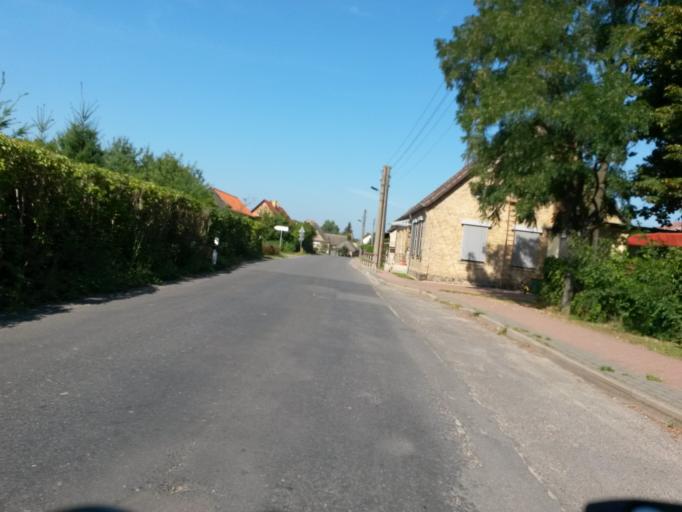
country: DE
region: Brandenburg
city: Templin
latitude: 53.0481
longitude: 13.4420
